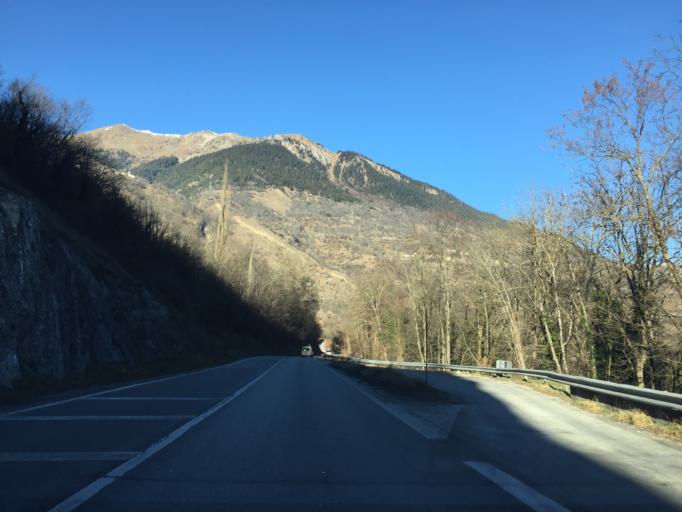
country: FR
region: Rhone-Alpes
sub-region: Departement de la Savoie
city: Aime
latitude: 45.5439
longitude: 6.6151
